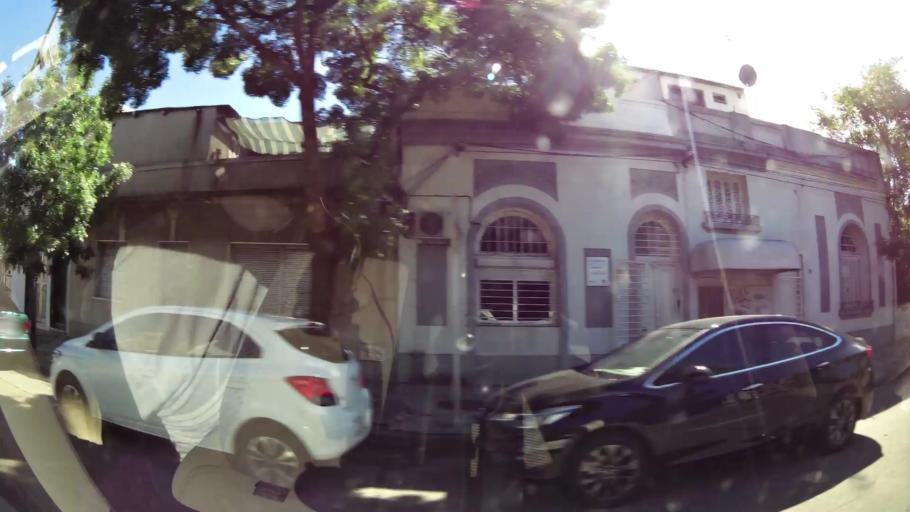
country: UY
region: Montevideo
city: Montevideo
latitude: -34.8749
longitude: -56.1883
